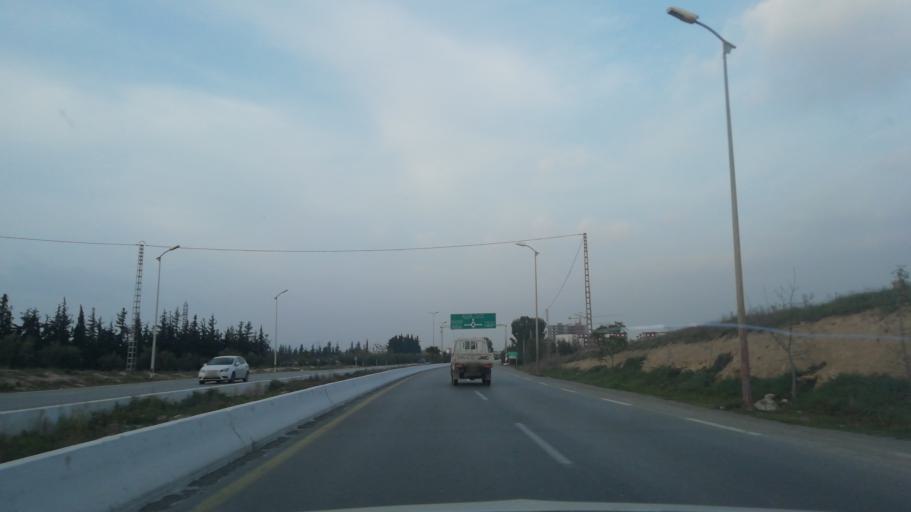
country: DZ
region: Sidi Bel Abbes
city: Sidi Bel Abbes
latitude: 35.2077
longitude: -0.6586
